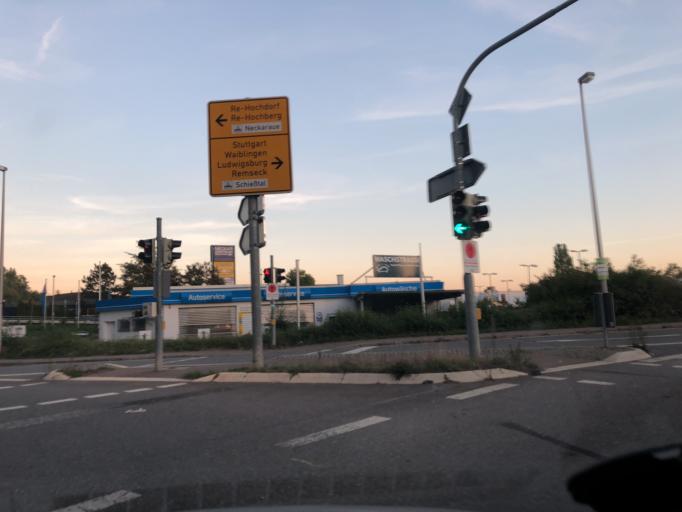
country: DE
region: Baden-Wuerttemberg
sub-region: Regierungsbezirk Stuttgart
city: Marbach am Neckar
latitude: 48.8907
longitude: 9.2707
